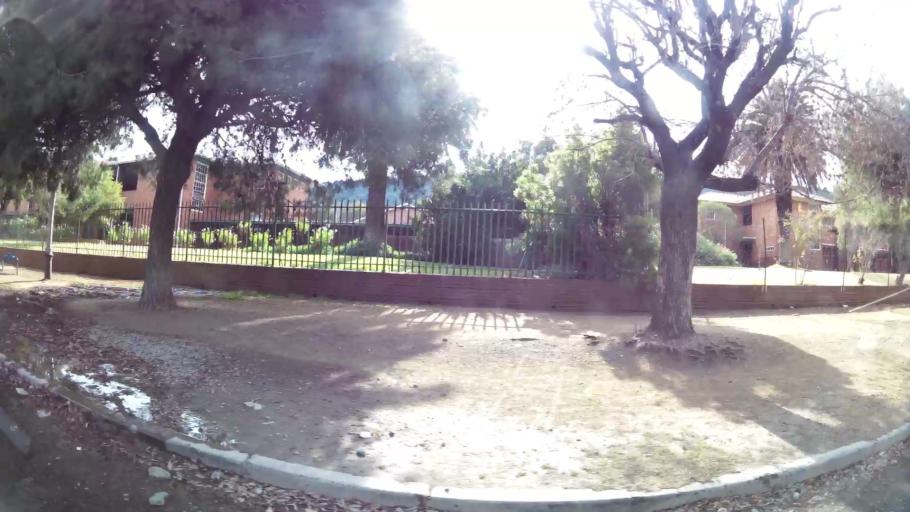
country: ZA
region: Orange Free State
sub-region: Mangaung Metropolitan Municipality
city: Bloemfontein
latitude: -29.1085
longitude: 26.2322
